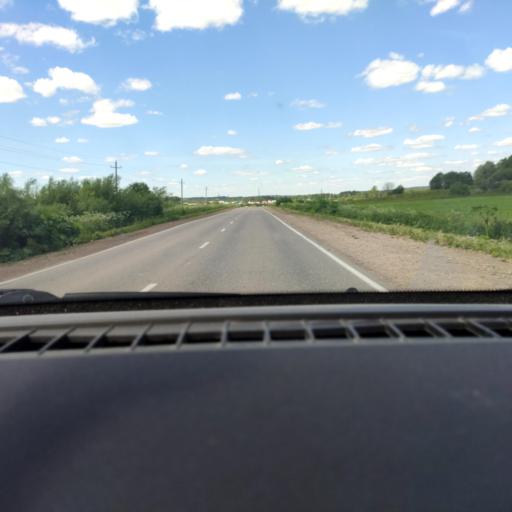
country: RU
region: Perm
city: Ust'-Kachka
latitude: 58.0719
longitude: 55.6243
